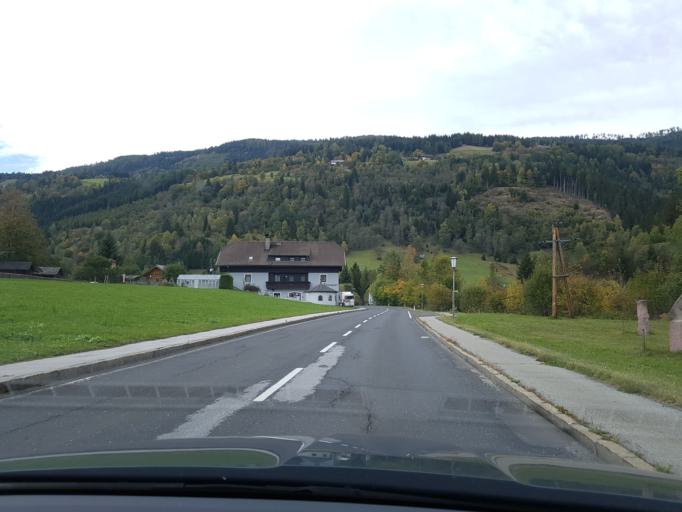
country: AT
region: Salzburg
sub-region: Politischer Bezirk Tamsweg
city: Ramingstein
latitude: 47.0770
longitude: 13.8165
